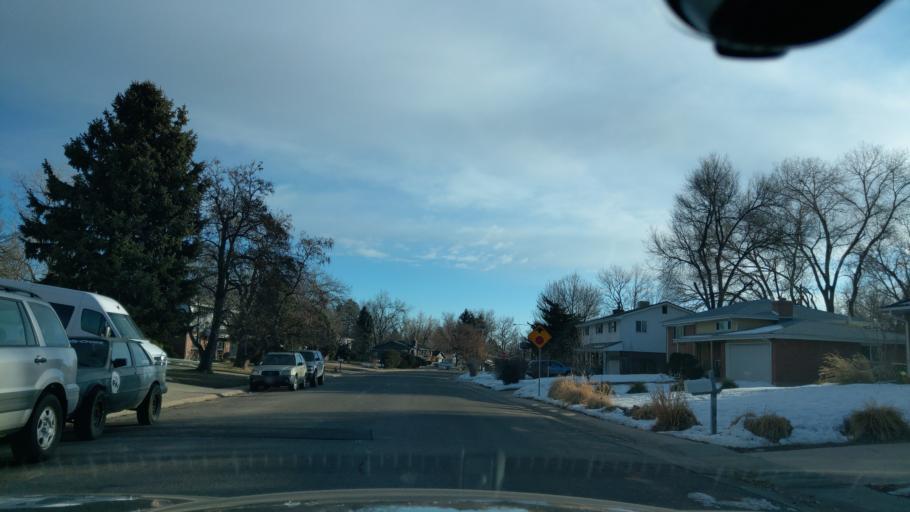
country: US
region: Colorado
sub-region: Jefferson County
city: Lakewood
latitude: 39.7305
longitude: -105.1163
